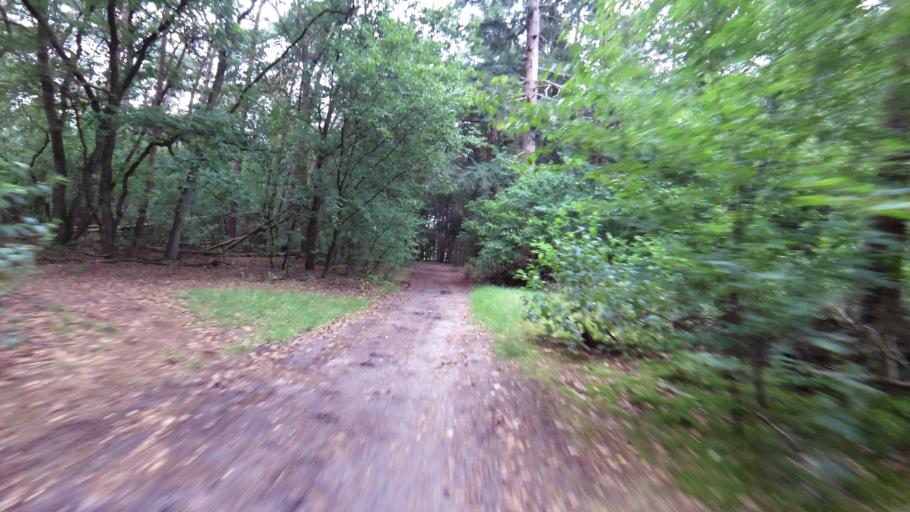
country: NL
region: Utrecht
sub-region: Gemeente Utrechtse Heuvelrug
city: Overberg
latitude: 52.0164
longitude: 5.5188
